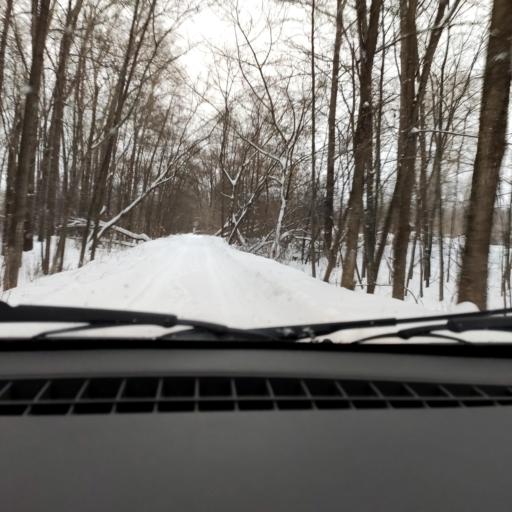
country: RU
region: Bashkortostan
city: Ufa
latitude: 54.7949
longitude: 56.1089
